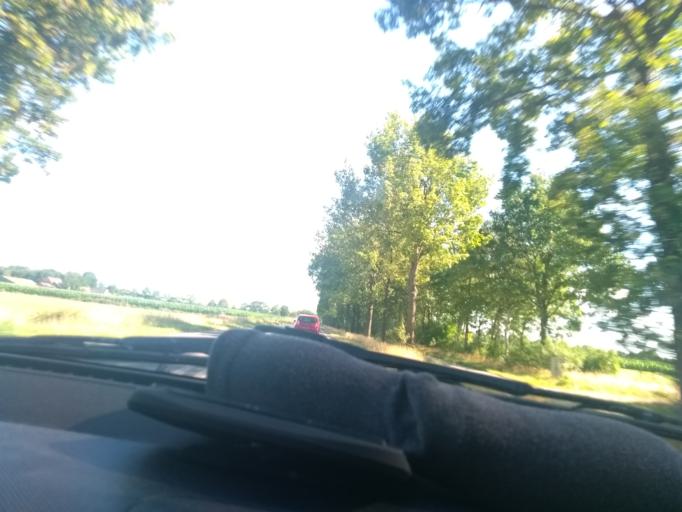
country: NL
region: Drenthe
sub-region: Gemeente Tynaarlo
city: Vries
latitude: 53.1305
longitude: 6.5002
